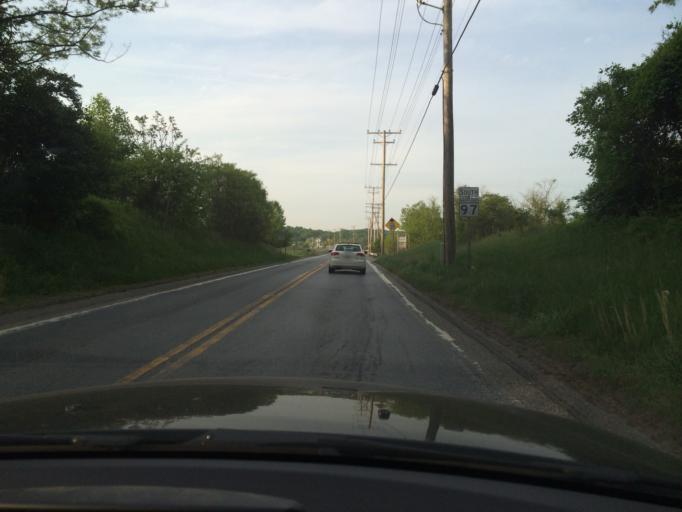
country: US
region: Maryland
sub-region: Carroll County
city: Sykesville
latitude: 39.3614
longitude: -77.0175
